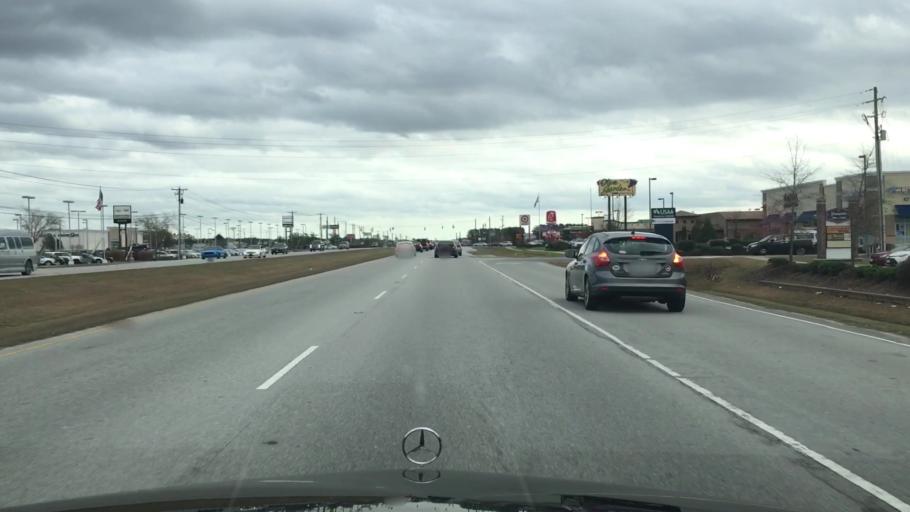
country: US
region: North Carolina
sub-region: Onslow County
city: Pumpkin Center
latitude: 34.7900
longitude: -77.4049
